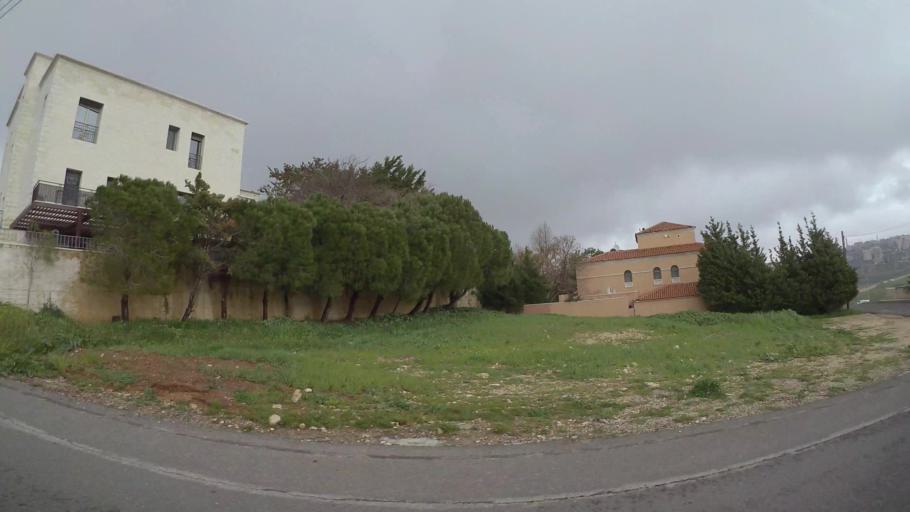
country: JO
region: Amman
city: Al Bunayyat ash Shamaliyah
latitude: 31.9332
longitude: 35.8828
